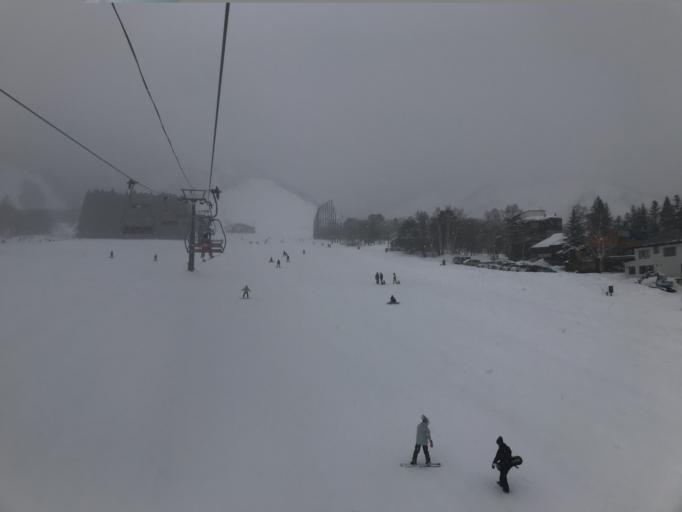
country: JP
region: Nagano
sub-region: Kitaazumi Gun
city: Hakuba
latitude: 36.7521
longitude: 137.8682
